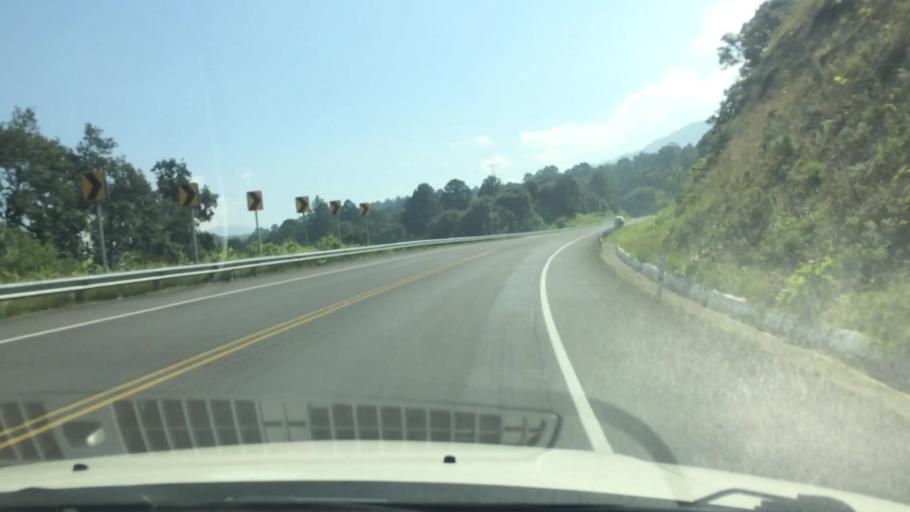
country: MX
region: Mexico
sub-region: Valle de Bravo
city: Santa Maria Pipioltepec (Pipioltepec)
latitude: 19.2200
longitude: -100.0952
